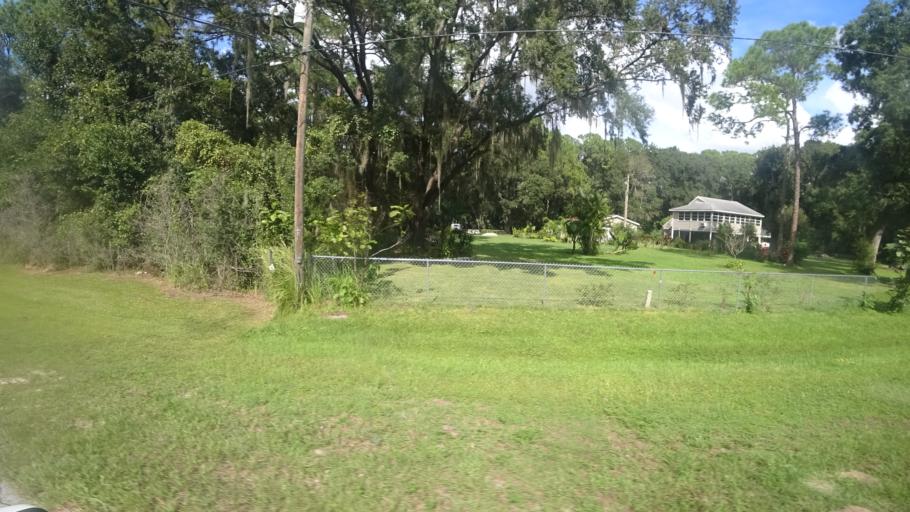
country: US
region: Florida
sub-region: Hillsborough County
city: Sun City Center
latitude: 27.6563
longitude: -82.3781
